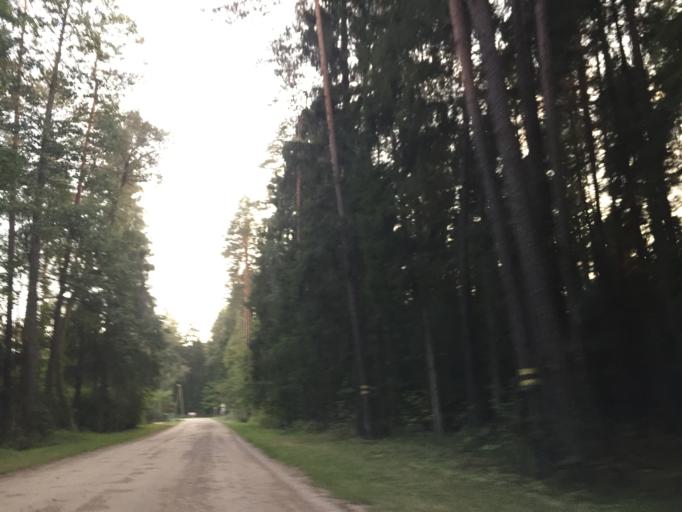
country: LV
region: Baldone
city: Baldone
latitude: 56.7527
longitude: 24.4046
